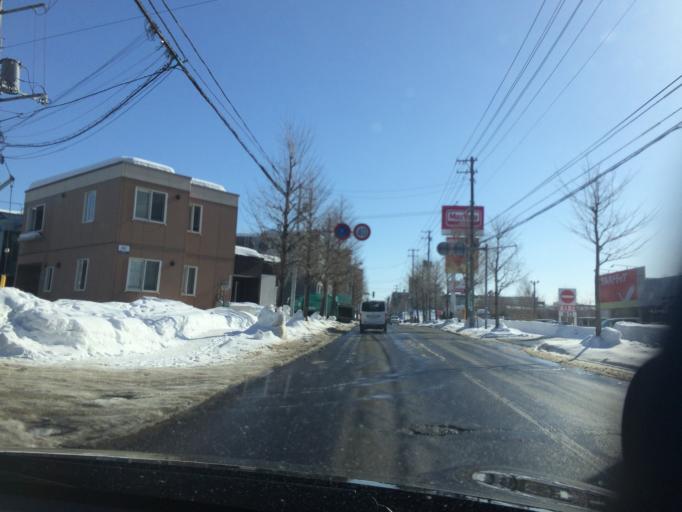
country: JP
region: Hokkaido
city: Sapporo
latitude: 43.0229
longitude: 141.4419
